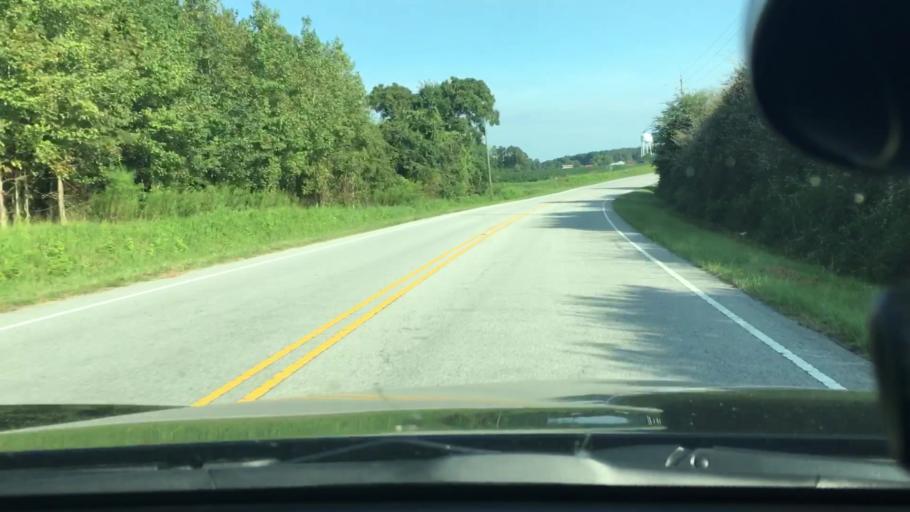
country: US
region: North Carolina
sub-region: Pitt County
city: Farmville
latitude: 35.7029
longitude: -77.5169
